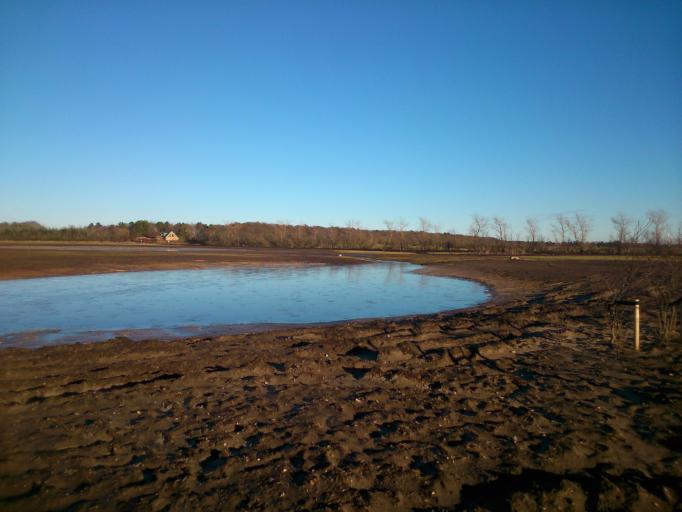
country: DK
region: Central Jutland
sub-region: Ringkobing-Skjern Kommune
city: Ringkobing
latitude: 56.0722
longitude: 8.2827
